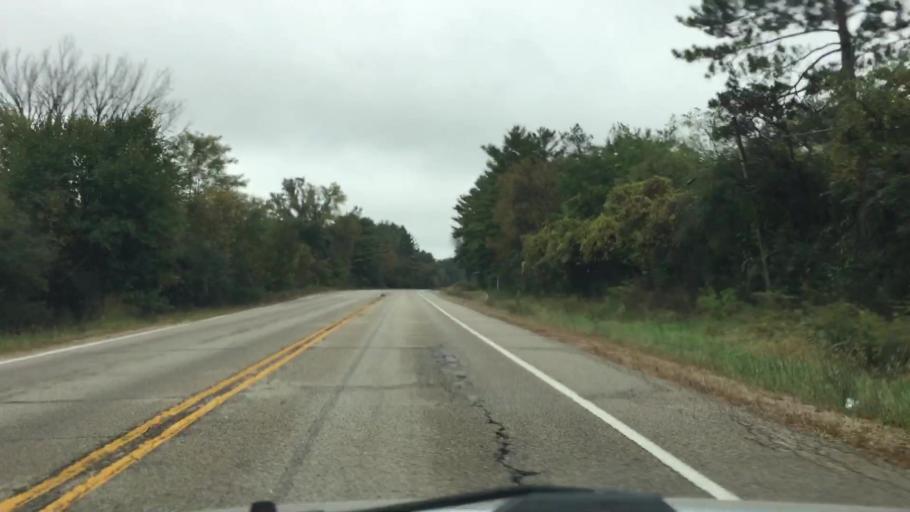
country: US
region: Wisconsin
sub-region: Rock County
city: Janesville
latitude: 42.7195
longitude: -89.0314
